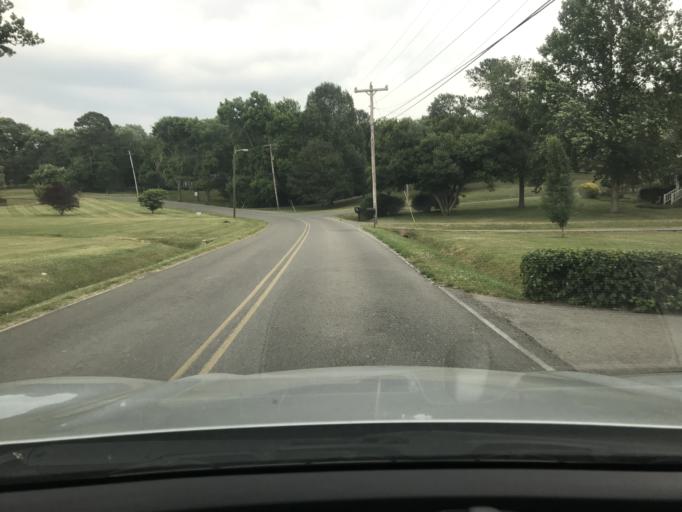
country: US
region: Tennessee
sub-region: Davidson County
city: Goodlettsville
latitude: 36.3049
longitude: -86.7178
